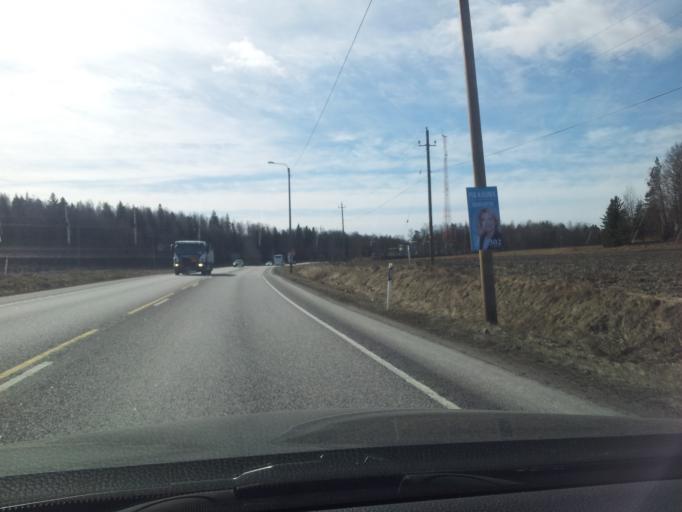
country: FI
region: Uusimaa
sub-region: Helsinki
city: Kirkkonummi
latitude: 60.1509
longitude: 24.5425
